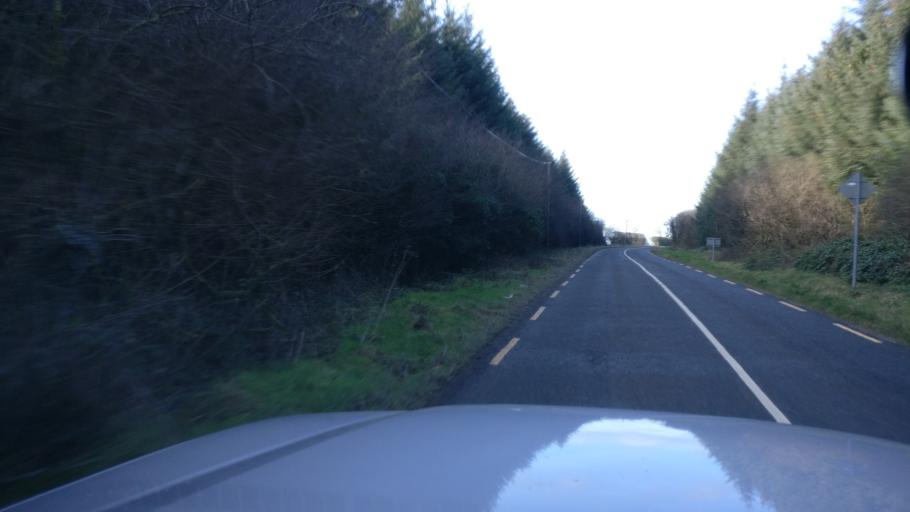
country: IE
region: Leinster
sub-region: Laois
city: Stradbally
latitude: 52.9152
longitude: -7.1852
